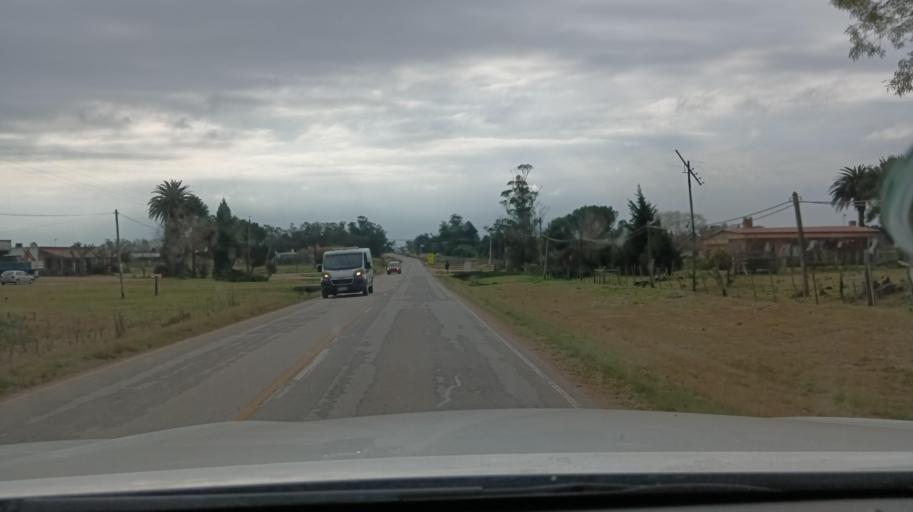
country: UY
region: Canelones
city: Sauce
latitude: -34.6323
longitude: -56.1097
